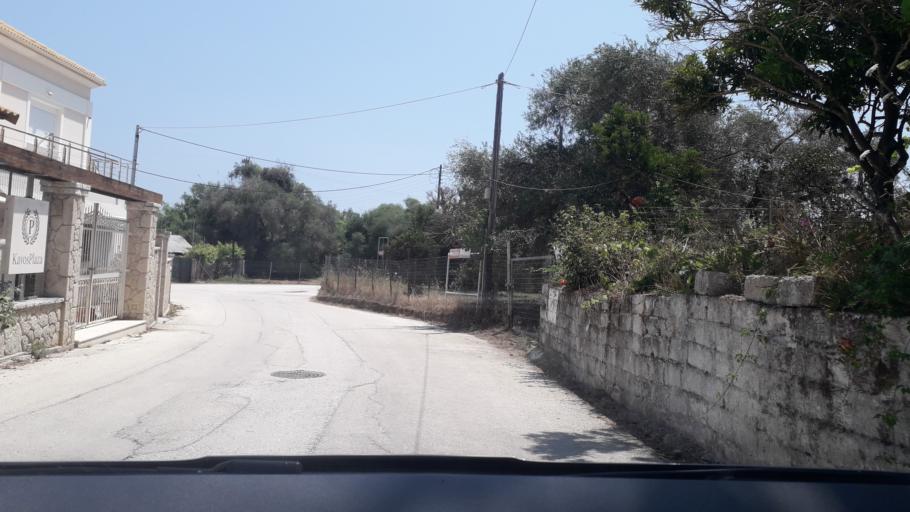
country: GR
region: Ionian Islands
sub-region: Nomos Kerkyras
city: Lefkimmi
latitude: 39.3802
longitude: 20.1152
